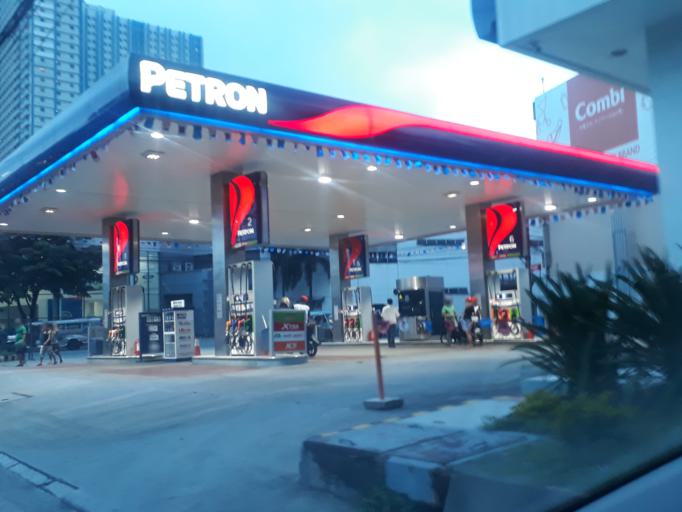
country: PH
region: Metro Manila
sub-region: City of Manila
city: Manila
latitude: 14.6194
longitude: 121.0032
